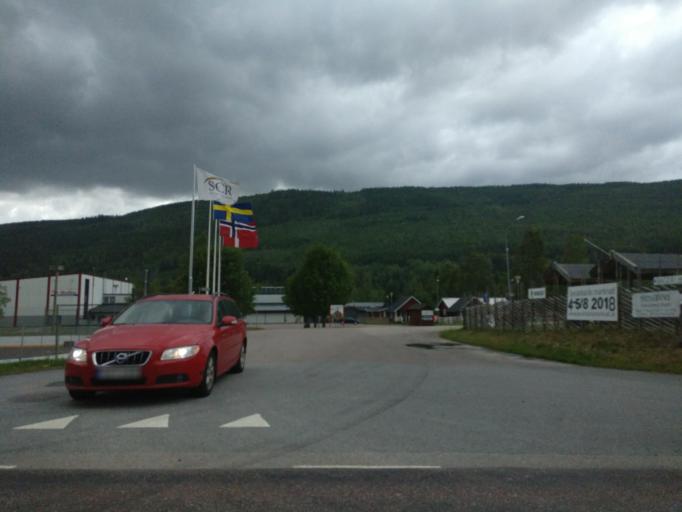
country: SE
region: Vaermland
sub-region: Torsby Kommun
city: Torsby
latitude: 60.7113
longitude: 12.8868
